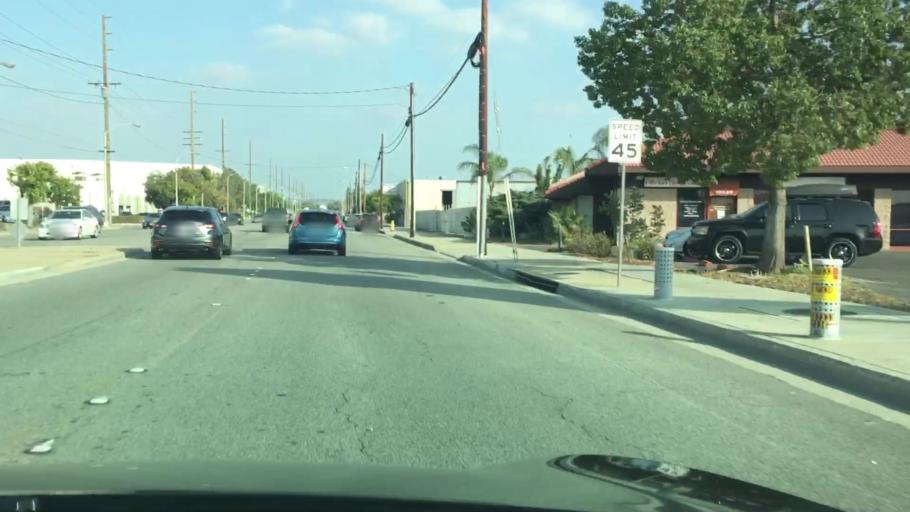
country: US
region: California
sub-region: Los Angeles County
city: La Mirada
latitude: 33.9024
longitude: -118.0367
